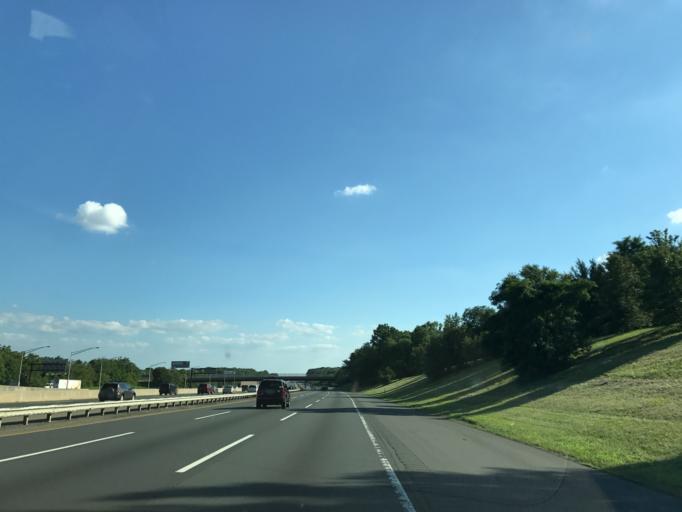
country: US
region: New Jersey
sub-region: Middlesex County
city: East Brunswick
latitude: 40.4142
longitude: -74.4478
